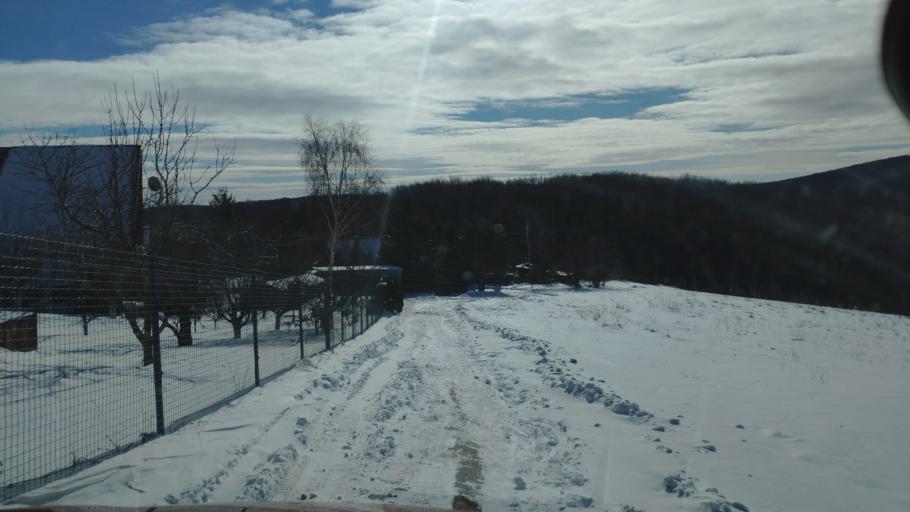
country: SK
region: Kosicky
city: Kosice
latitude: 48.7592
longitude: 21.2108
